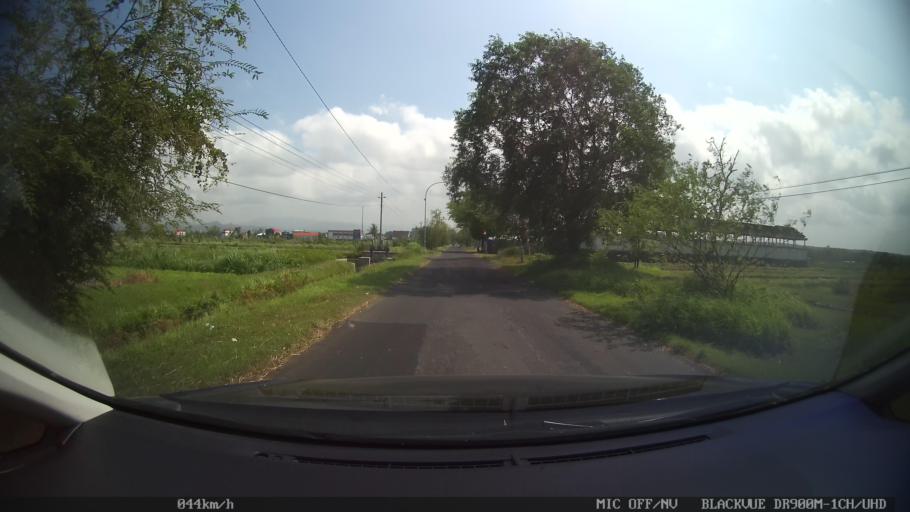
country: ID
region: Daerah Istimewa Yogyakarta
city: Srandakan
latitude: -7.8993
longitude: 110.1524
